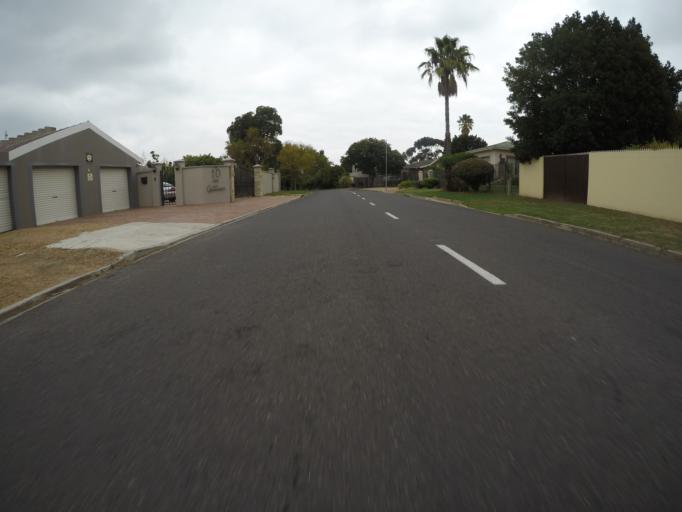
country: ZA
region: Western Cape
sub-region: City of Cape Town
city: Kraaifontein
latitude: -33.8648
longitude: 18.6478
